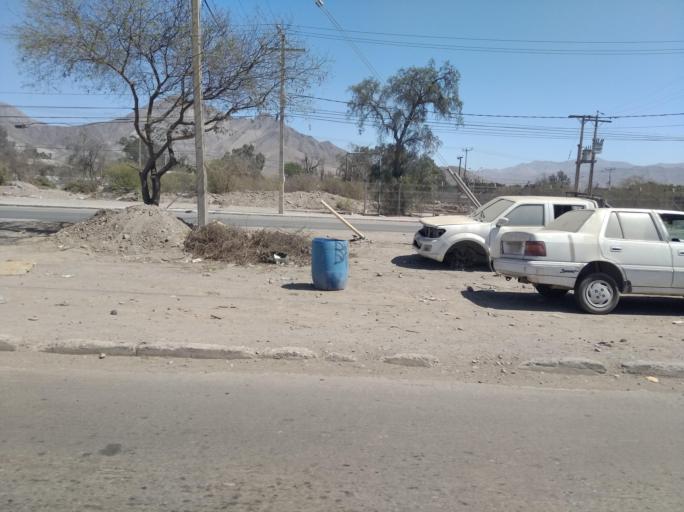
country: CL
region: Atacama
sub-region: Provincia de Copiapo
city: Copiapo
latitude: -27.4131
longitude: -70.2816
